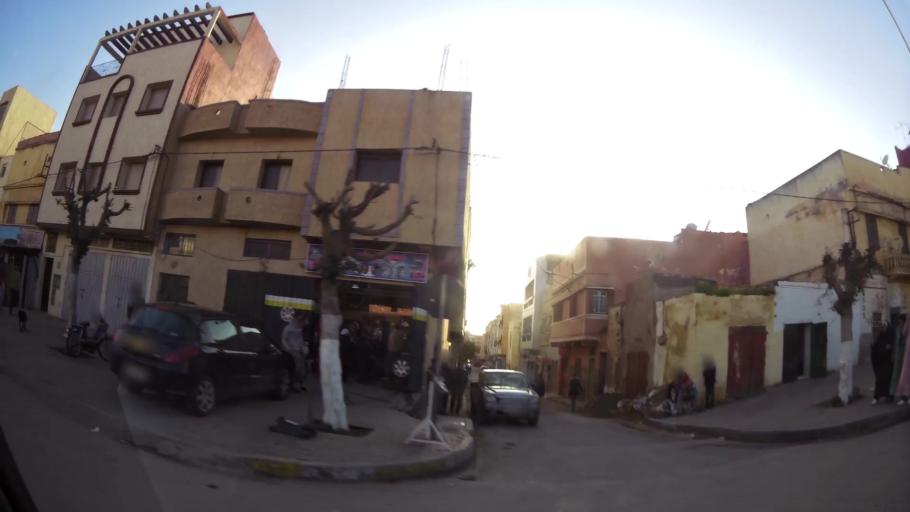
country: MA
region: Chaouia-Ouardigha
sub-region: Settat Province
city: Settat
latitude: 33.0038
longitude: -7.6159
